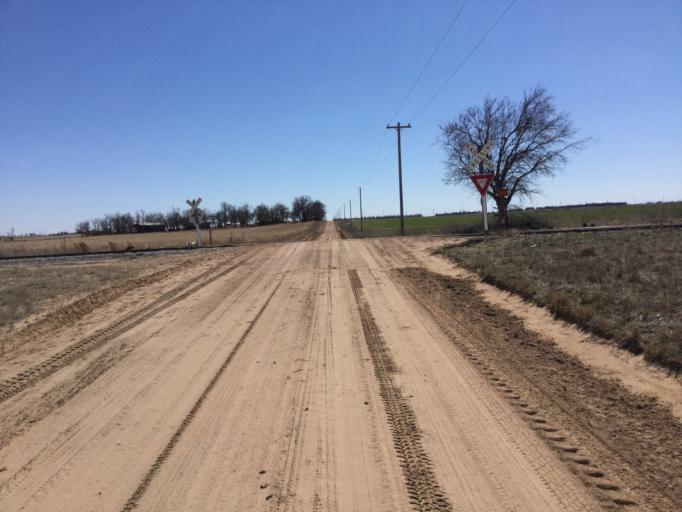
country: US
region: Kansas
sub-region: Barber County
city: Medicine Lodge
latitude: 37.4520
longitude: -98.4830
